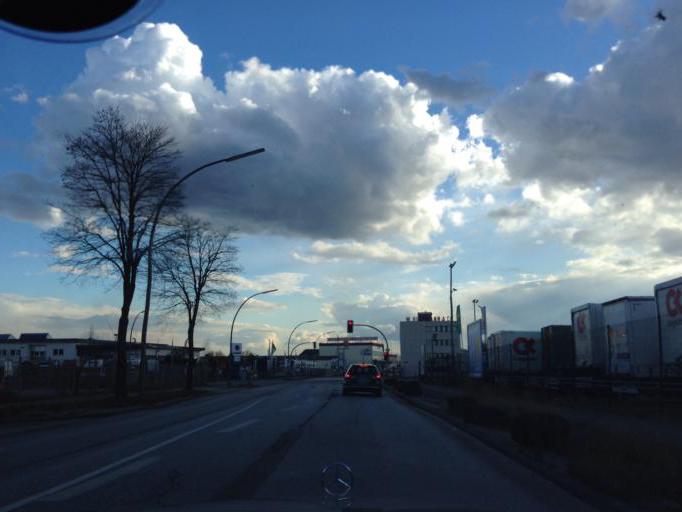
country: DE
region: Hamburg
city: Wandsbek
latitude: 53.5268
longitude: 10.0930
